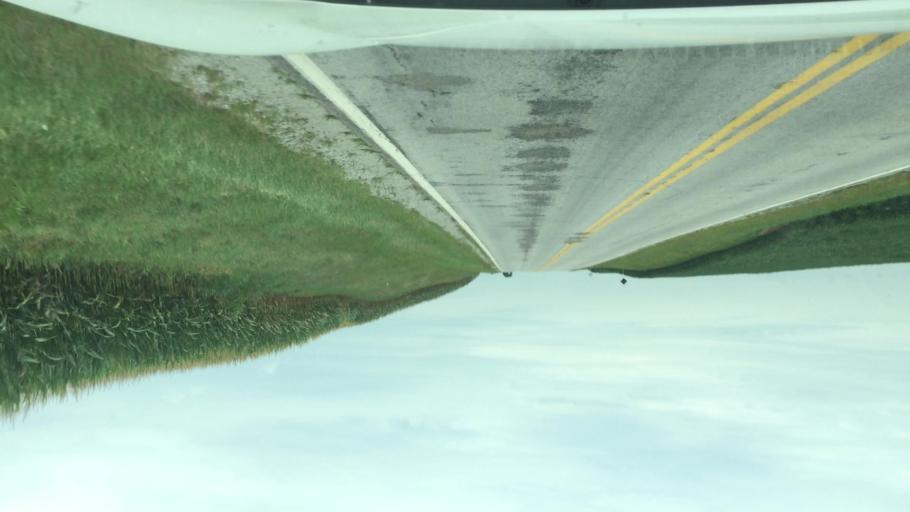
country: US
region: Ohio
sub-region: Clark County
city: Northridge
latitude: 39.9671
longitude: -83.6788
